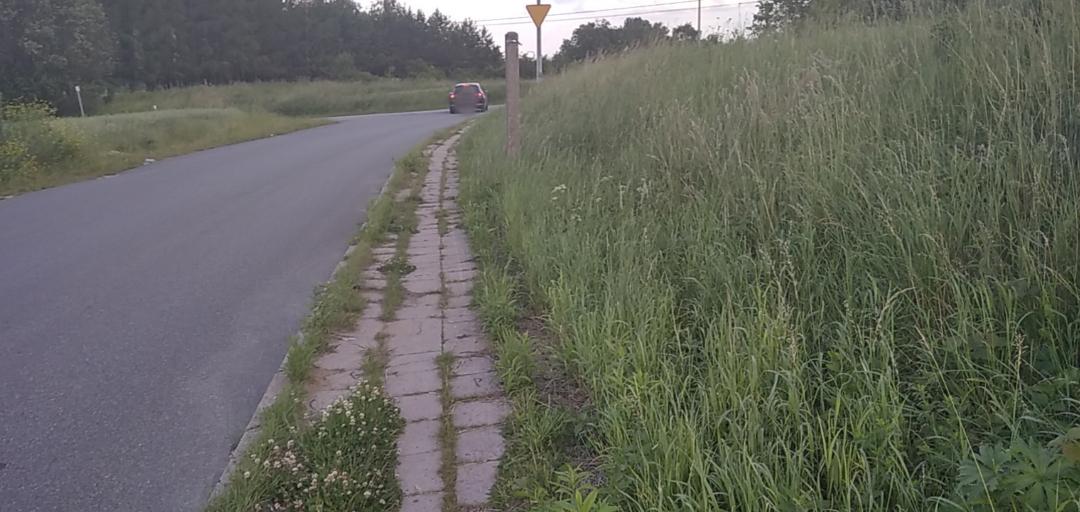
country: PL
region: Silesian Voivodeship
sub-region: Powiat bedzinski
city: Sarnow
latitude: 50.4091
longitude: 19.1399
